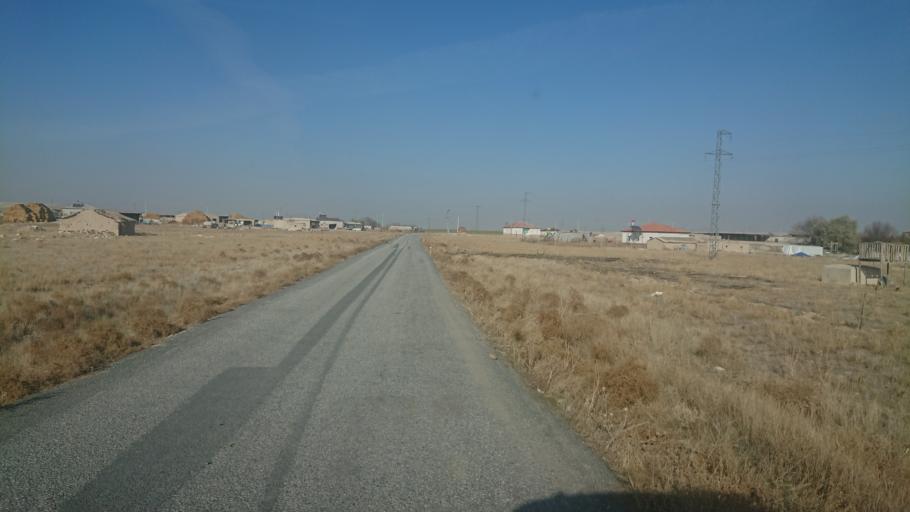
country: TR
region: Aksaray
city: Sultanhani
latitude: 38.0355
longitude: 33.6058
